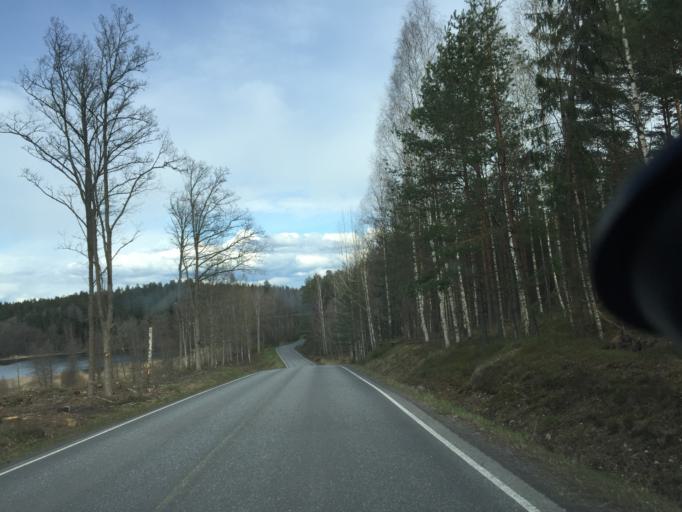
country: FI
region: Varsinais-Suomi
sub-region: Salo
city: Saerkisalo
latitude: 60.0027
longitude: 23.0908
